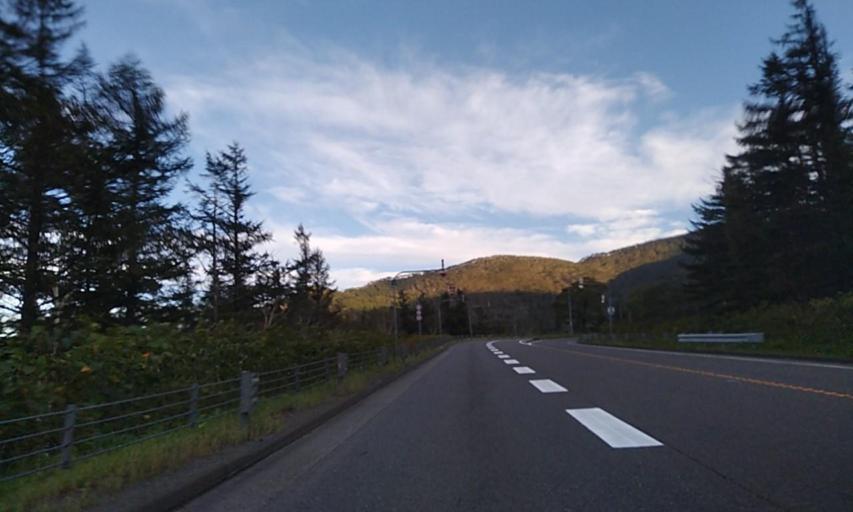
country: JP
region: Hokkaido
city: Otofuke
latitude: 42.9585
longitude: 142.7937
